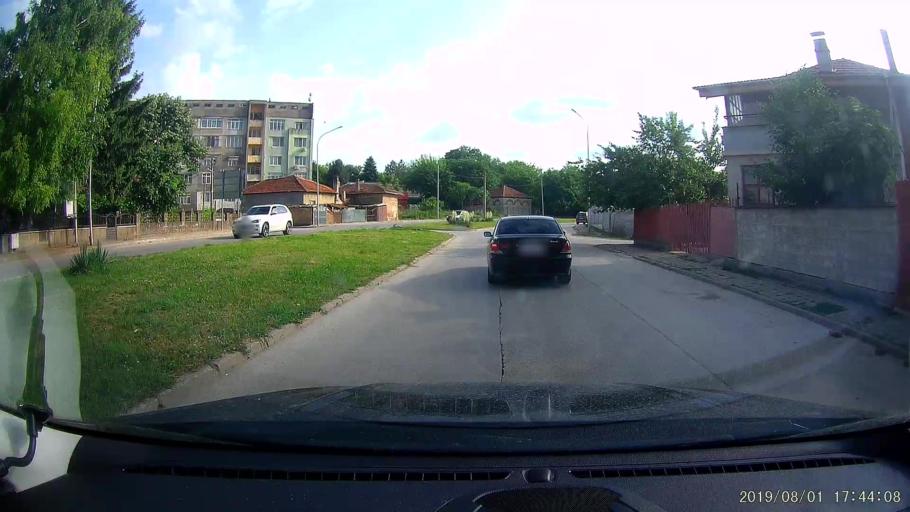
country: BG
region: Silistra
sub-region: Obshtina Silistra
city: Silistra
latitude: 44.1109
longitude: 27.2712
